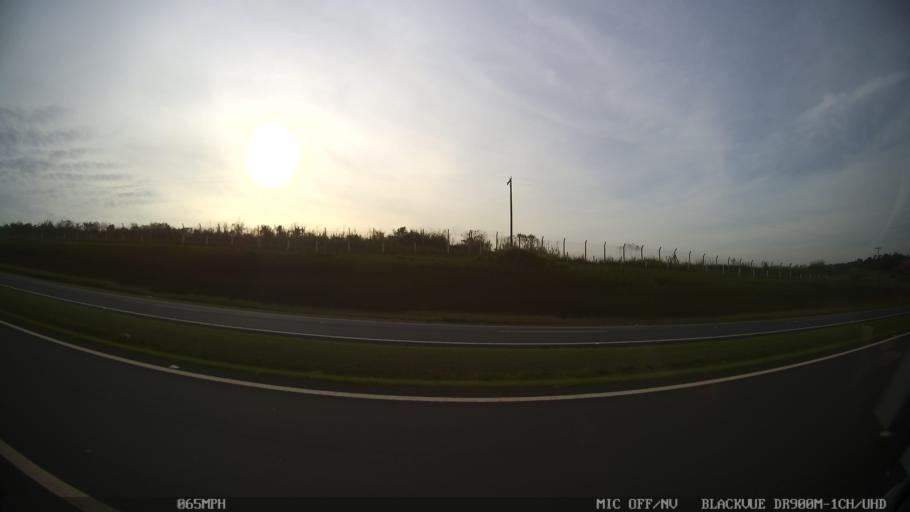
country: BR
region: Sao Paulo
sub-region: Iracemapolis
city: Iracemapolis
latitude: -22.6257
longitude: -47.4966
